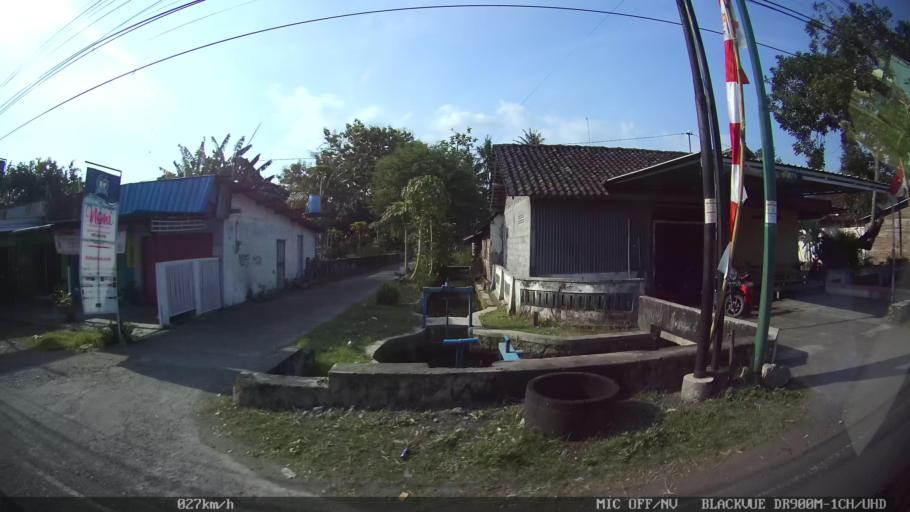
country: ID
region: Daerah Istimewa Yogyakarta
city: Pandak
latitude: -7.9016
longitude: 110.2994
